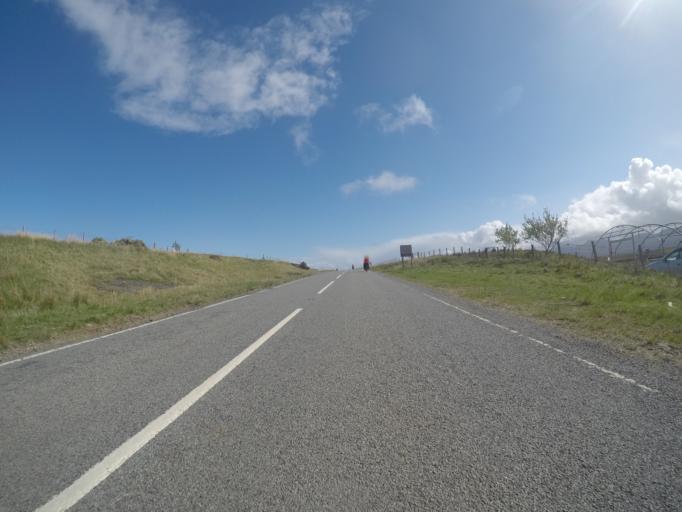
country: GB
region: Scotland
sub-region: Highland
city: Portree
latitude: 57.6194
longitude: -6.1958
